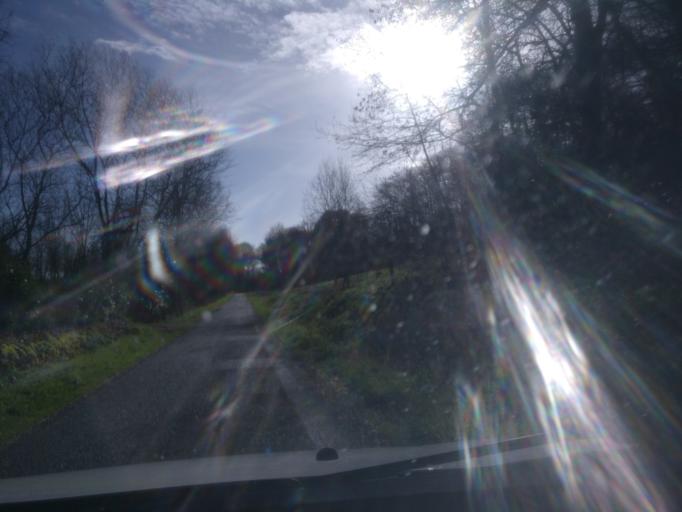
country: FR
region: Brittany
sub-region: Departement d'Ille-et-Vilaine
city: Antrain
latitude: 48.4938
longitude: -1.4959
